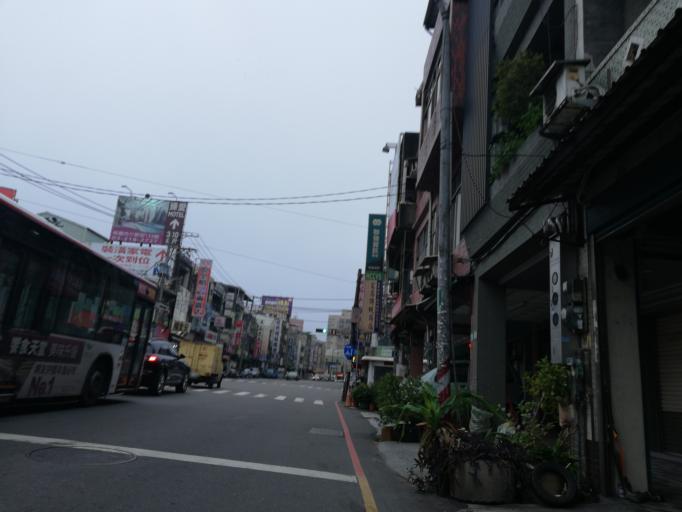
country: TW
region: Taiwan
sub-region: Taoyuan
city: Taoyuan
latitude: 24.9857
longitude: 121.3107
